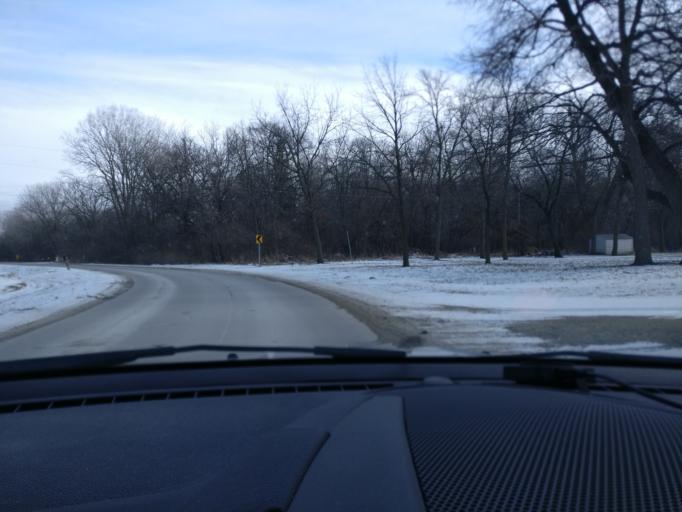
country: US
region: Nebraska
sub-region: Dodge County
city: Fremont
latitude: 41.4132
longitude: -96.5212
